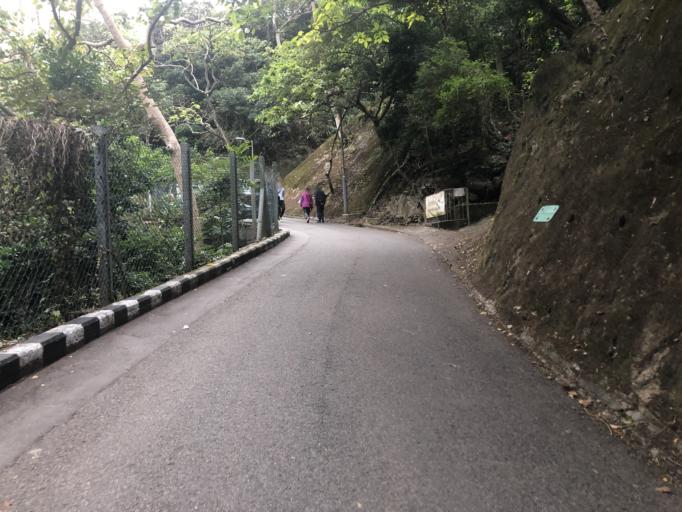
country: HK
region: Wanchai
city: Wan Chai
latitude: 22.2836
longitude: 114.2118
